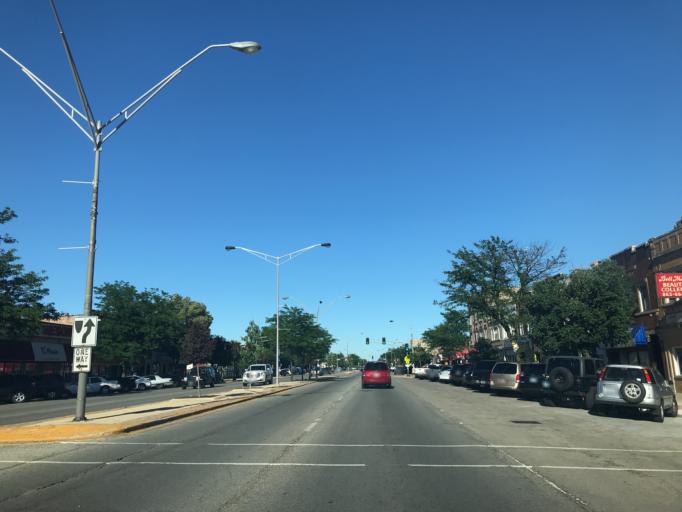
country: US
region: Illinois
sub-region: Cook County
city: Cicero
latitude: 41.8509
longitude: -87.7675
